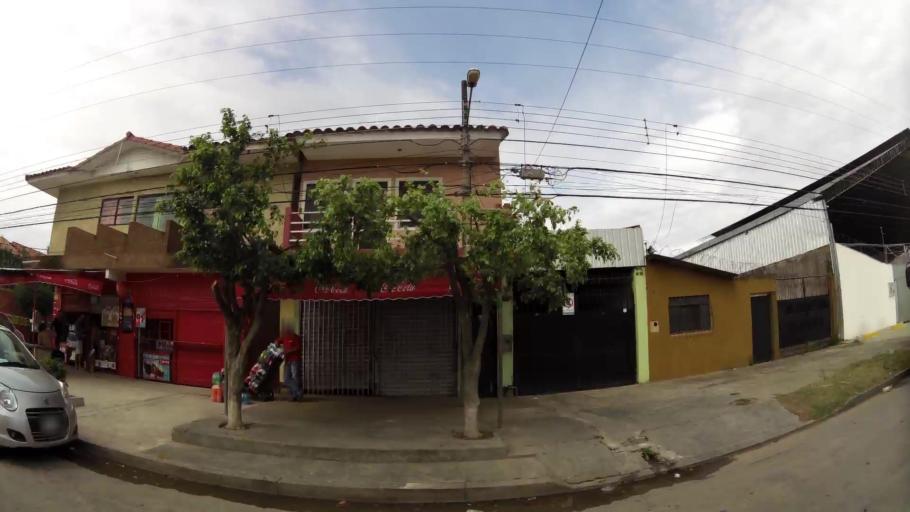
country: BO
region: Santa Cruz
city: Santa Cruz de la Sierra
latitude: -17.7804
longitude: -63.2150
